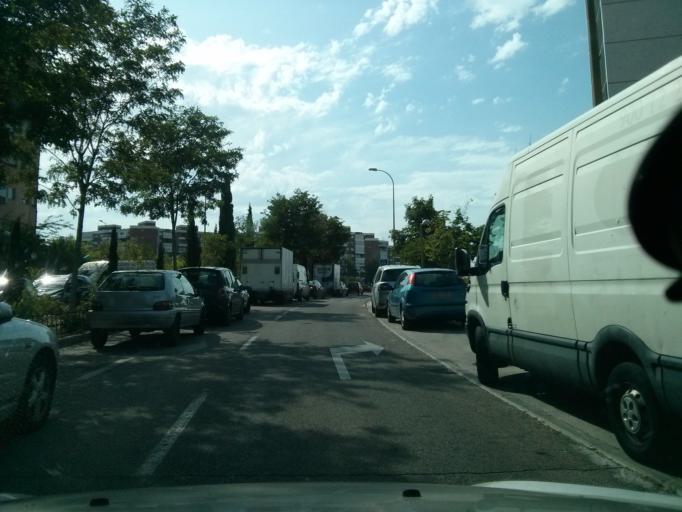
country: ES
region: Madrid
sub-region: Provincia de Madrid
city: Pinar de Chamartin
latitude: 40.4868
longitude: -3.6574
